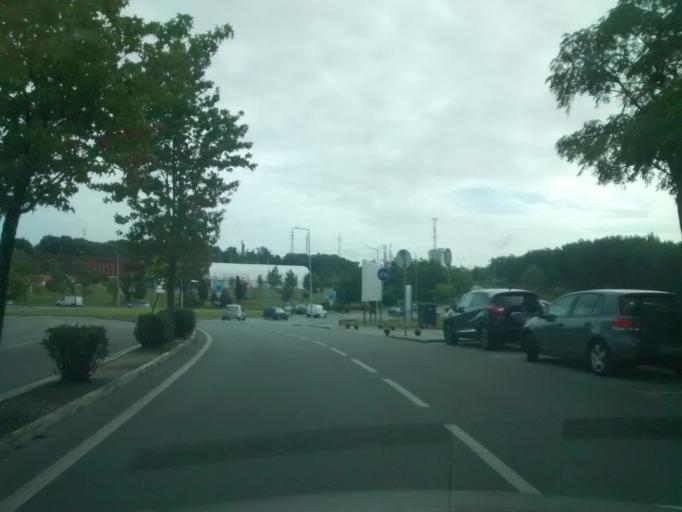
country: PT
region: Aveiro
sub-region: Aveiro
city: Aveiro
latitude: 40.6395
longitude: -8.6408
